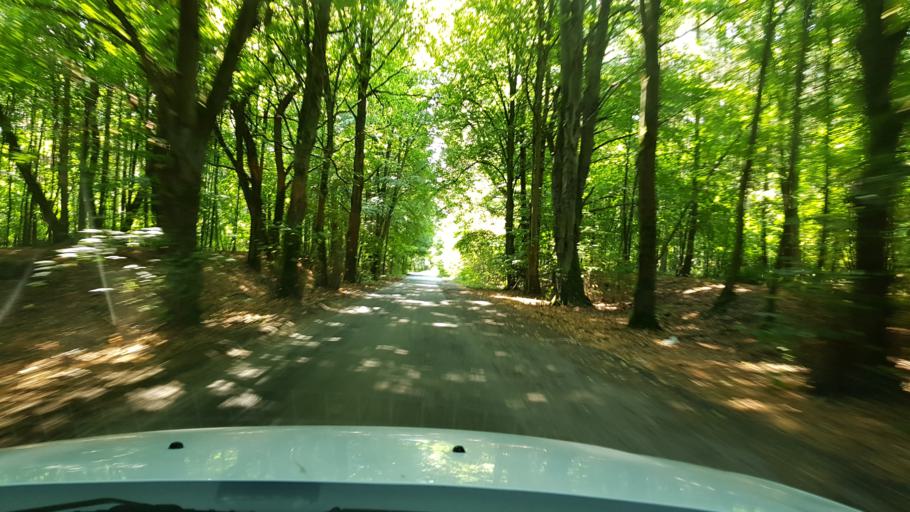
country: PL
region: West Pomeranian Voivodeship
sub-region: Powiat gryfinski
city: Chojna
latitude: 52.9417
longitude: 14.5136
